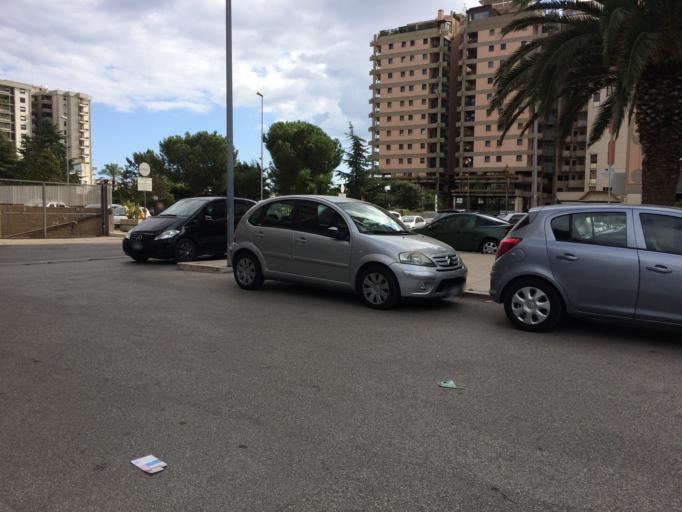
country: IT
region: Apulia
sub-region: Provincia di Bari
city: Bari
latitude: 41.0975
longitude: 16.8533
